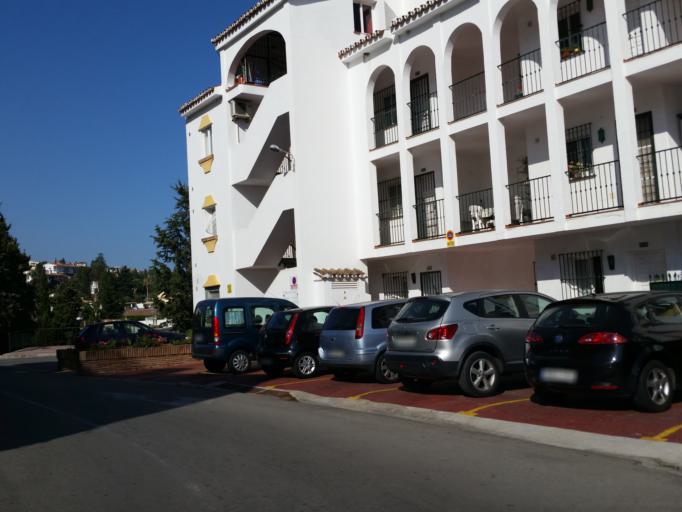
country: ES
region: Andalusia
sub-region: Provincia de Malaga
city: Fuengirola
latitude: 36.5645
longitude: -4.6080
